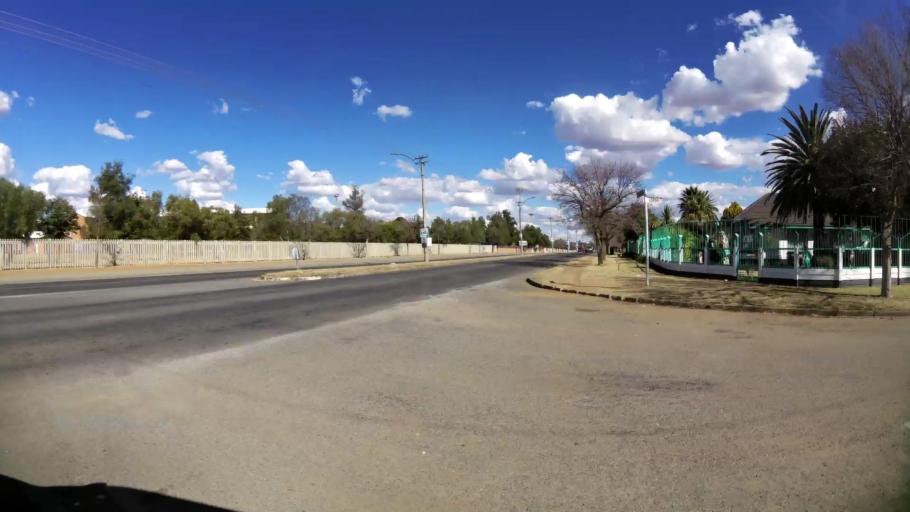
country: ZA
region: North-West
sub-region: Dr Kenneth Kaunda District Municipality
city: Klerksdorp
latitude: -26.8595
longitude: 26.6428
